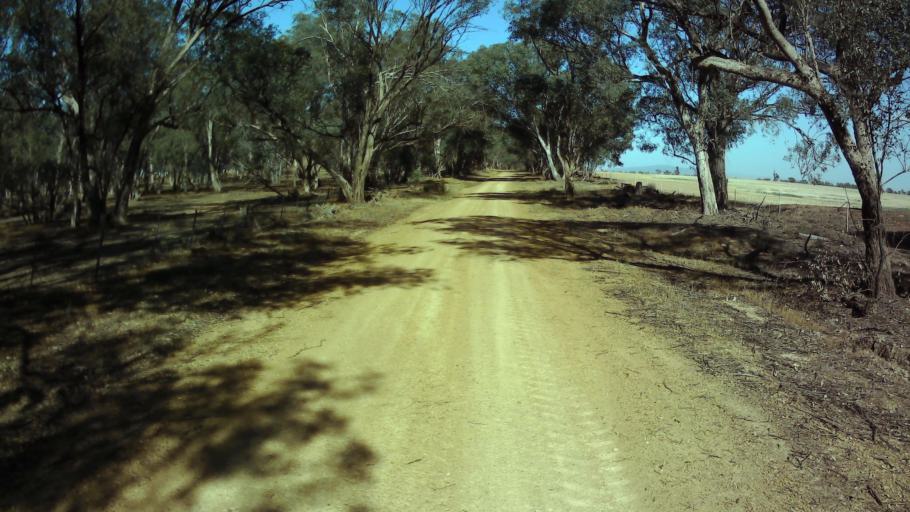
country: AU
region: New South Wales
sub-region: Weddin
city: Grenfell
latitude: -34.0497
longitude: 148.2971
